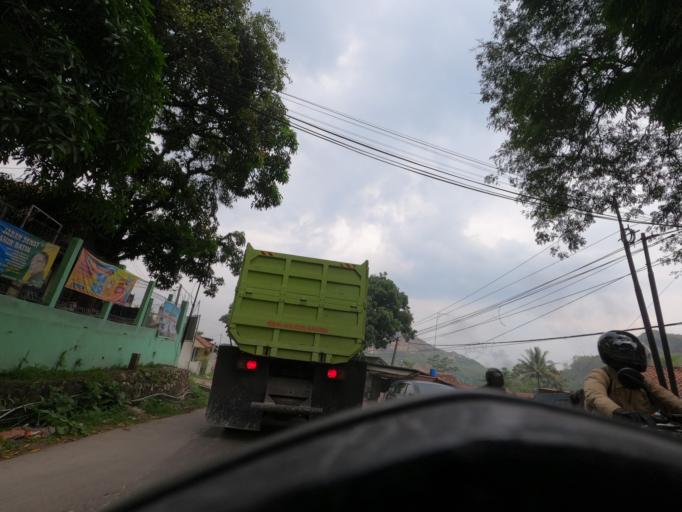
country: ID
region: West Java
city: Padalarang
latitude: -6.8309
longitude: 107.4331
